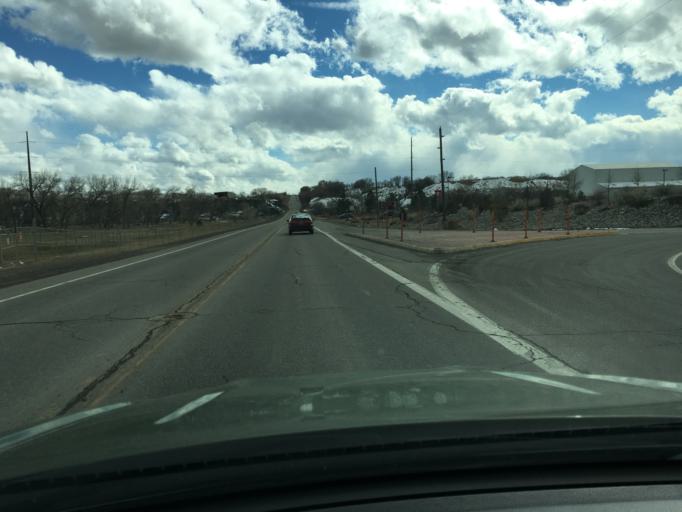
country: US
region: Colorado
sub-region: Mesa County
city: Clifton
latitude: 39.0593
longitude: -108.4595
